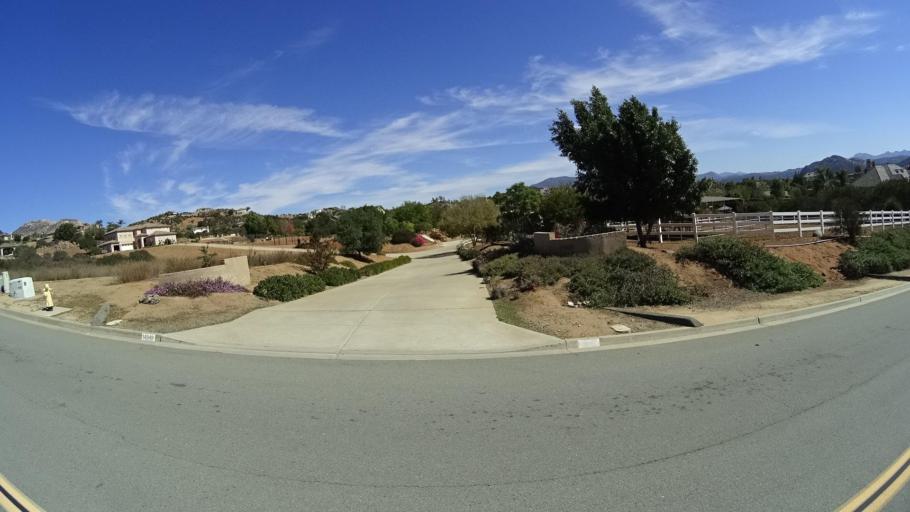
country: US
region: California
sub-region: San Diego County
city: Harbison Canyon
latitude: 32.8770
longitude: -116.8449
